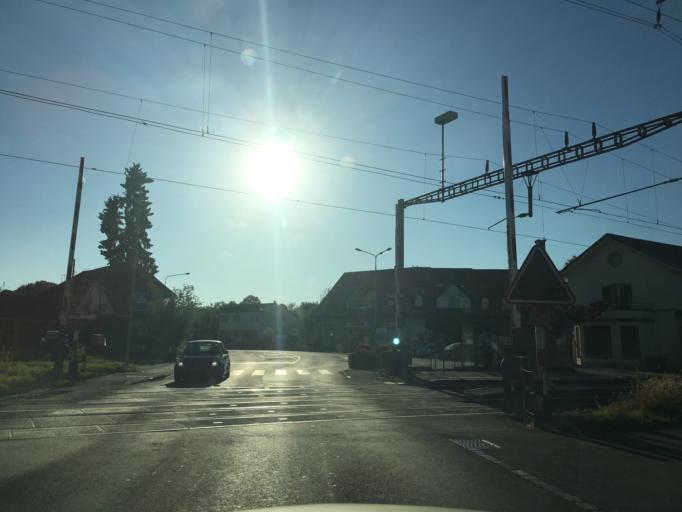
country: CH
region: Vaud
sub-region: Lavaux-Oron District
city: Oron-la-ville
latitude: 46.5705
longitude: 6.8163
